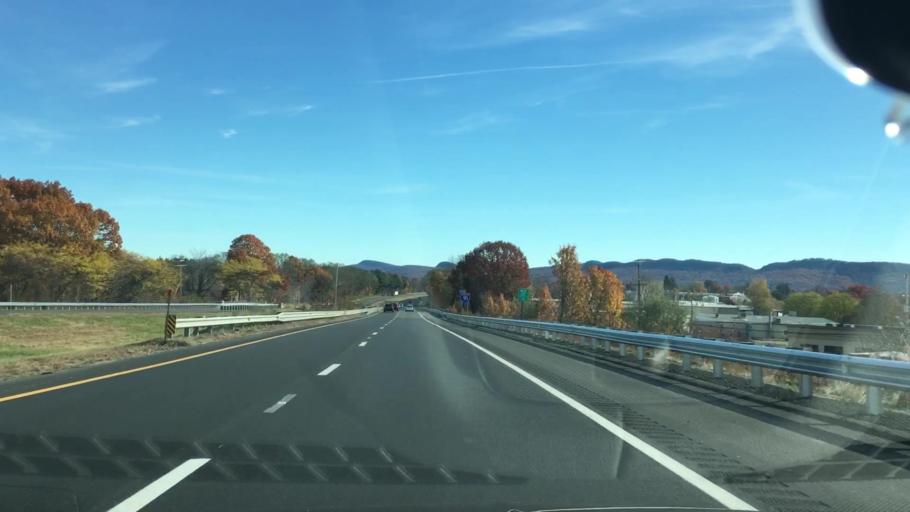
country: US
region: Massachusetts
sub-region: Hampshire County
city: Northampton
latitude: 42.3392
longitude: -72.6359
